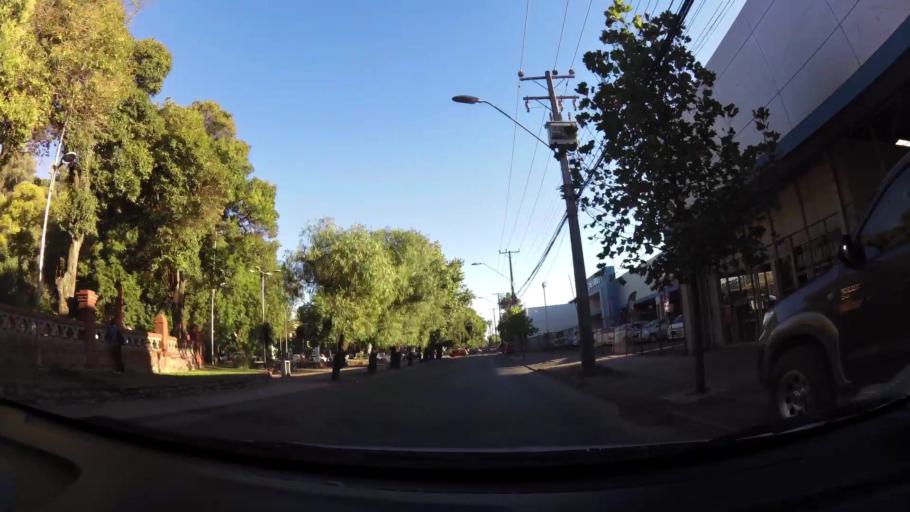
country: CL
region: Maule
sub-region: Provincia de Curico
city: Curico
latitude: -34.9825
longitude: -71.2347
